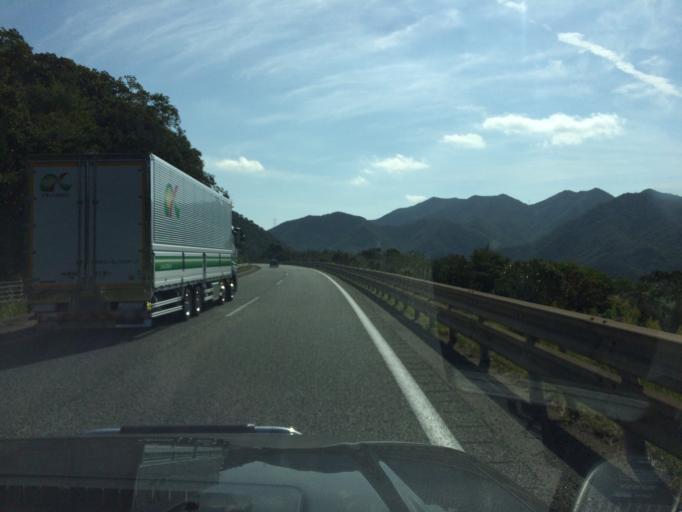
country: JP
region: Hyogo
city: Sasayama
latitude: 35.0087
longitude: 135.1604
